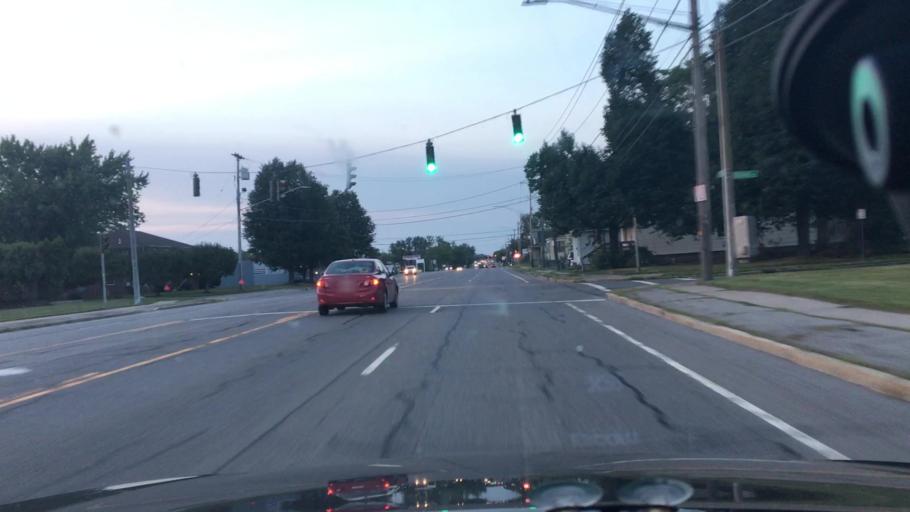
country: US
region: New York
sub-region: Erie County
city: West Seneca
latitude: 42.8571
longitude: -78.7545
